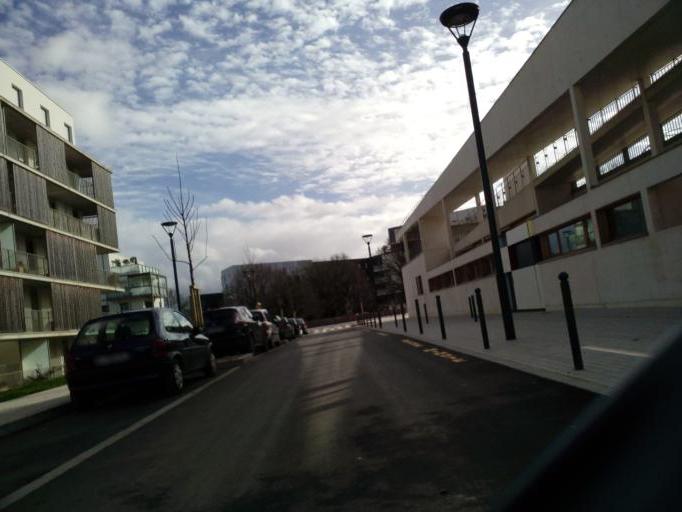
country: FR
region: Brittany
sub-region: Departement d'Ille-et-Vilaine
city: Saint-Gregoire
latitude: 48.1343
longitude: -1.6984
